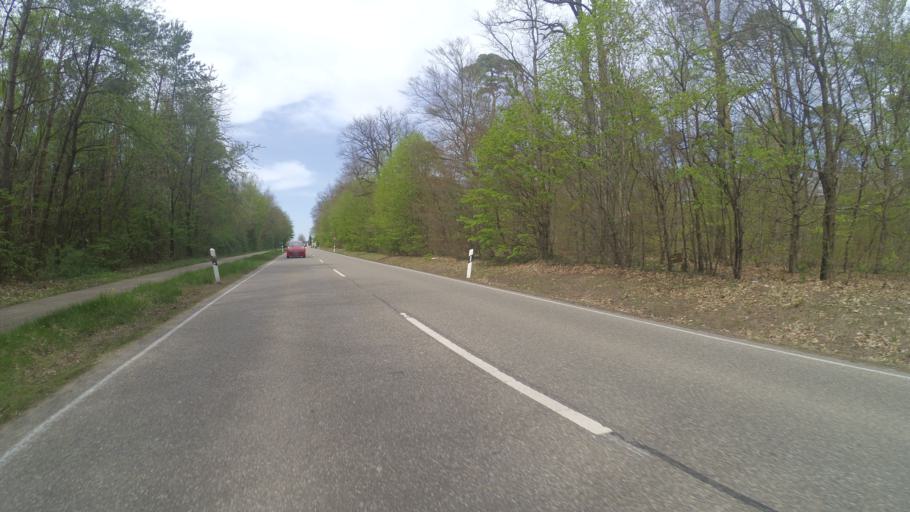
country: DE
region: Rheinland-Pfalz
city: Waldmohr
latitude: 49.3628
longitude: 7.3257
